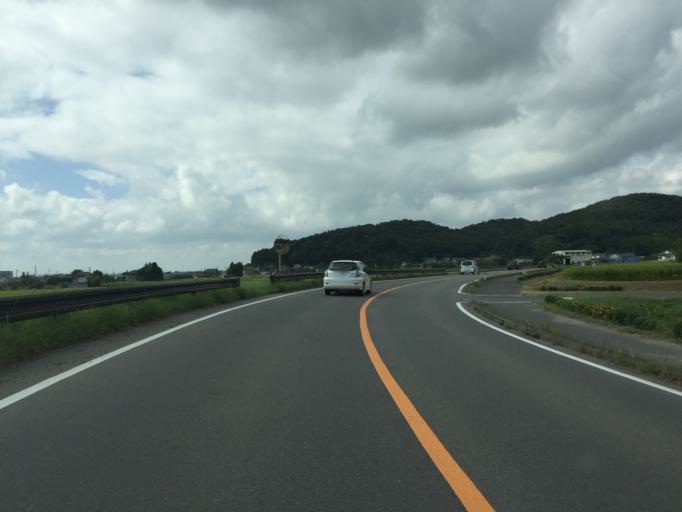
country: JP
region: Fukushima
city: Motomiya
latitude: 37.4933
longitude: 140.3752
